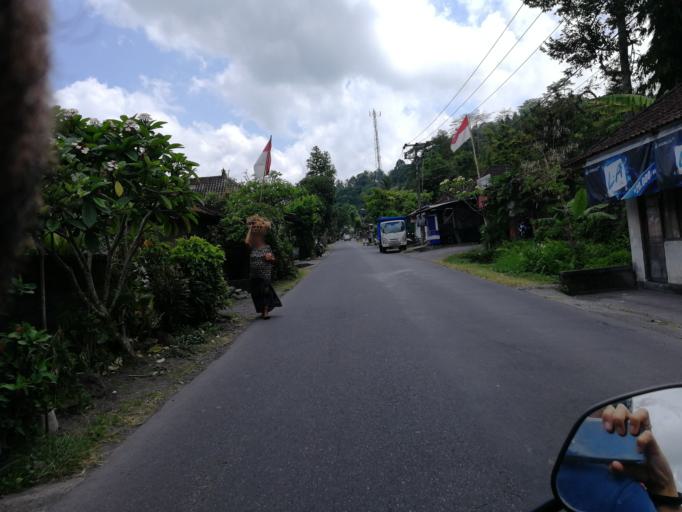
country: ID
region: Bali
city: Banjar Wangsian
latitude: -8.4570
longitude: 115.4507
